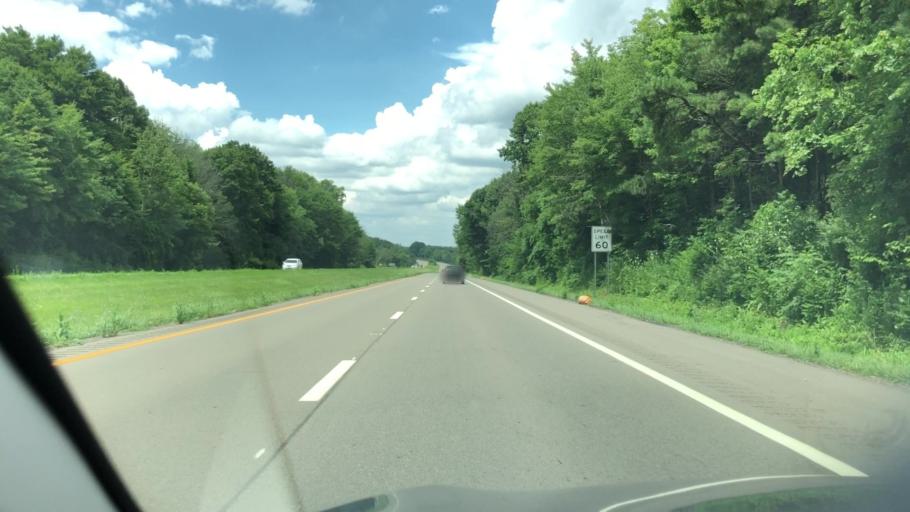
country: US
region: Ohio
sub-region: Stark County
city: Massillon
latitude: 40.8395
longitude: -81.5525
